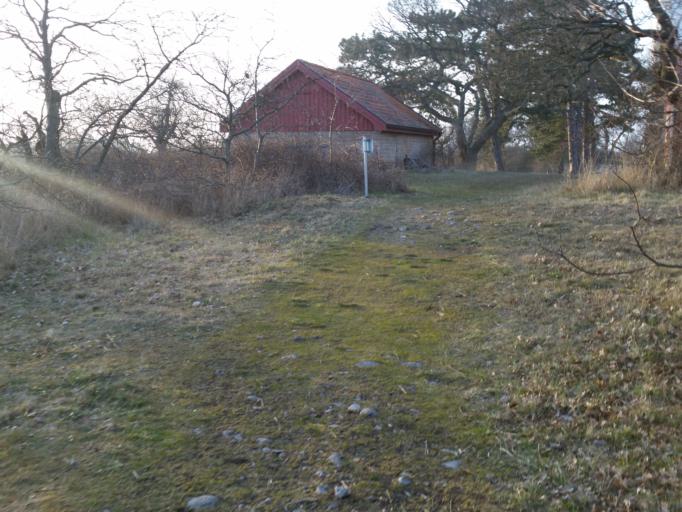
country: SE
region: Kalmar
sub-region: Vasterviks Kommun
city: Vaestervik
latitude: 57.3660
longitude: 17.0981
